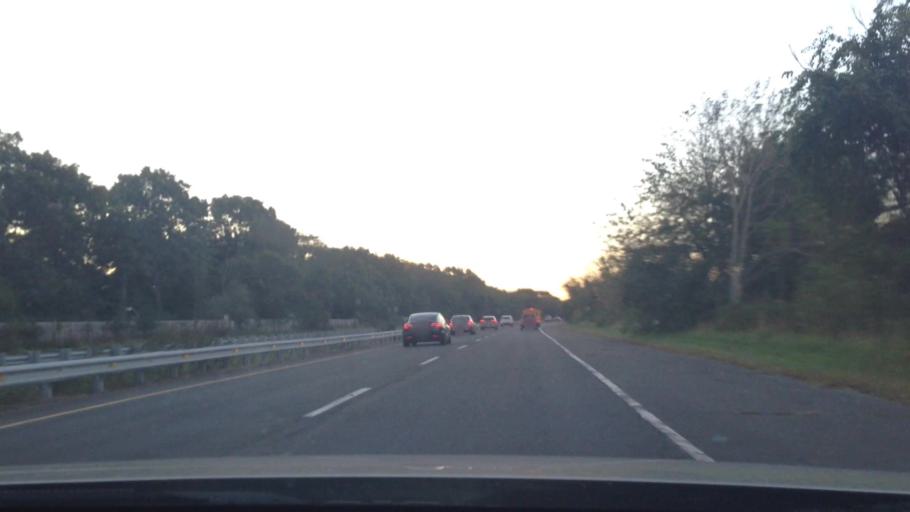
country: US
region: New York
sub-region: Suffolk County
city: Coram
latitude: 40.9015
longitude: -73.0048
